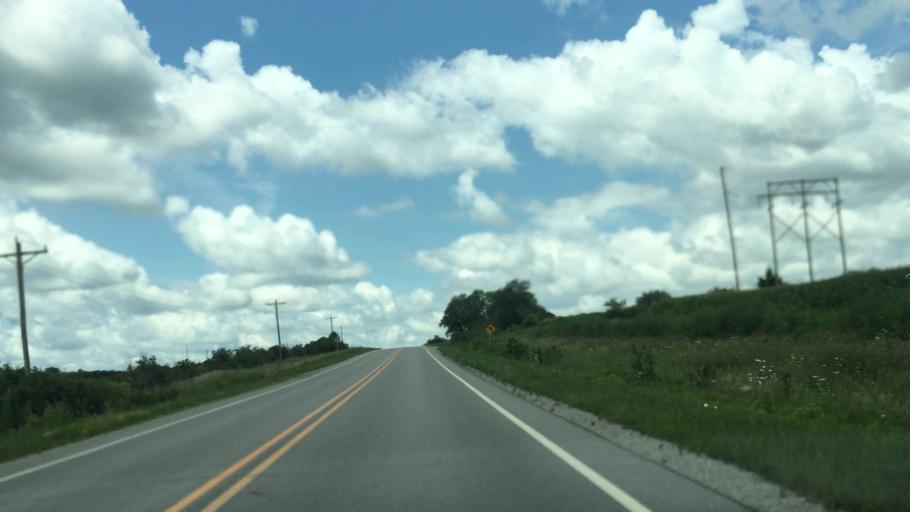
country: US
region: Iowa
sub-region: Johnson County
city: Solon
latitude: 41.8382
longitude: -91.4284
